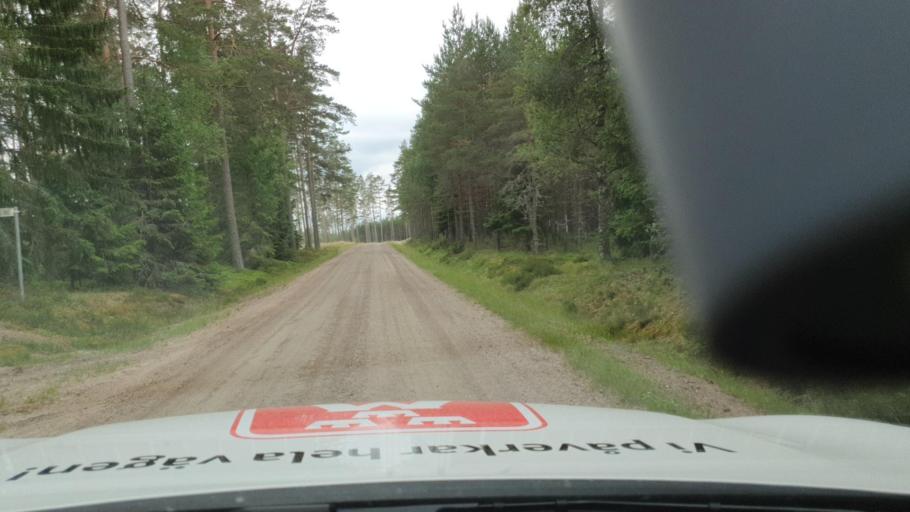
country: SE
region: Vaestra Goetaland
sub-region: Tidaholms Kommun
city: Olofstorp
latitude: 58.1882
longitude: 14.1129
